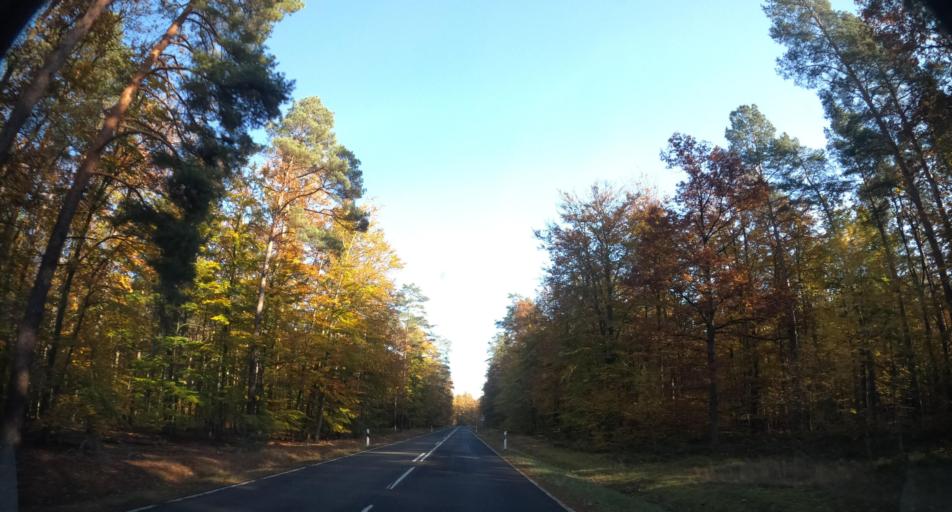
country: PL
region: West Pomeranian Voivodeship
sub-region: Powiat policki
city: Nowe Warpno
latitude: 53.6206
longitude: 14.2829
